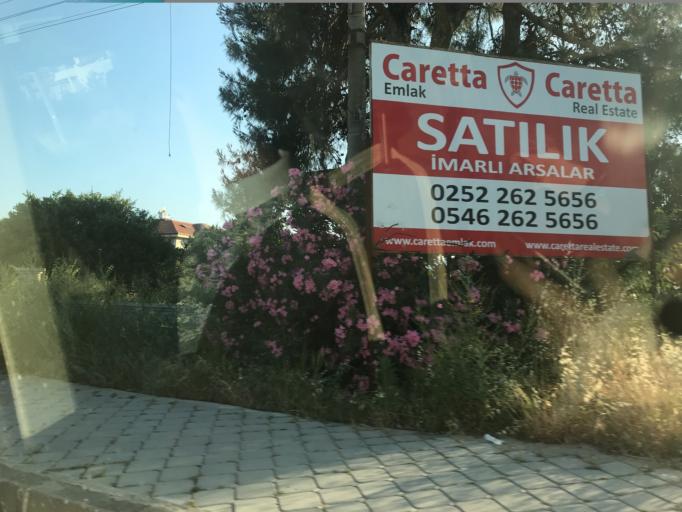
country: TR
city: Dalyan
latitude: 36.9715
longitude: 28.6866
